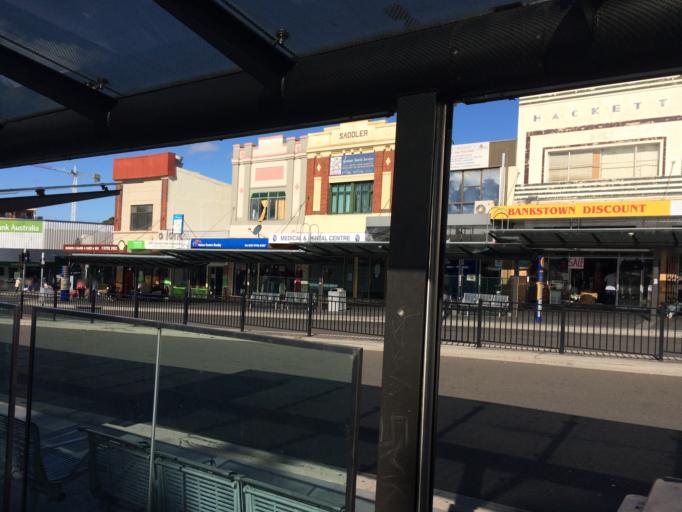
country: AU
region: New South Wales
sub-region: Bankstown
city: Bankstown
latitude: -33.9182
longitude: 151.0346
